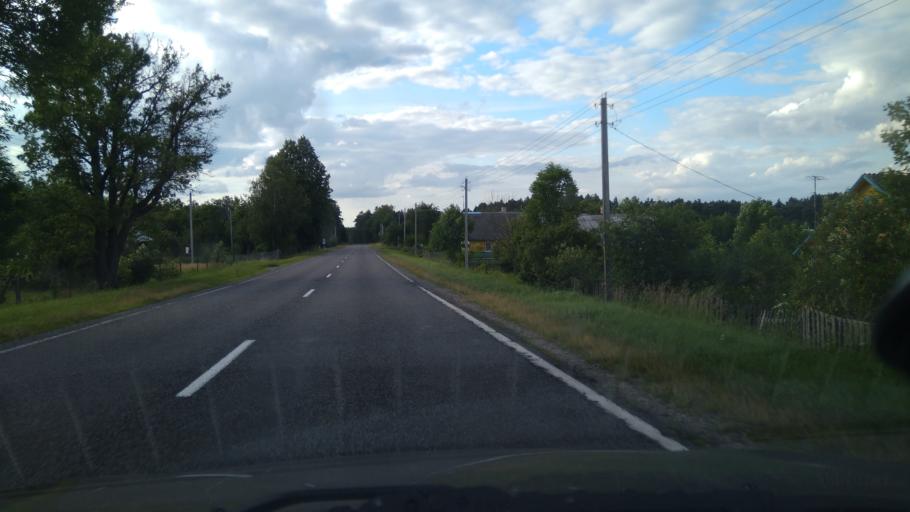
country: BY
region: Grodnenskaya
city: Masty
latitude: 53.3388
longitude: 24.6711
